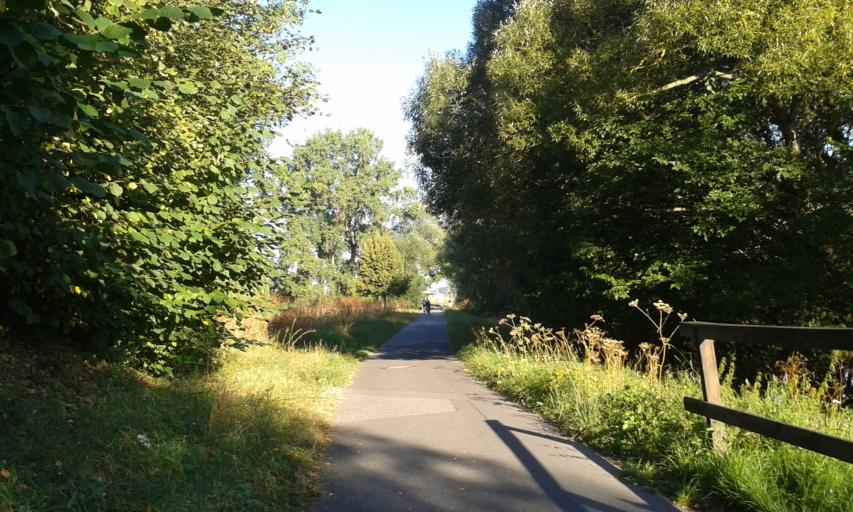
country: DE
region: Bavaria
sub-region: Upper Franconia
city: Bischberg
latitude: 49.9094
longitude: 10.8403
